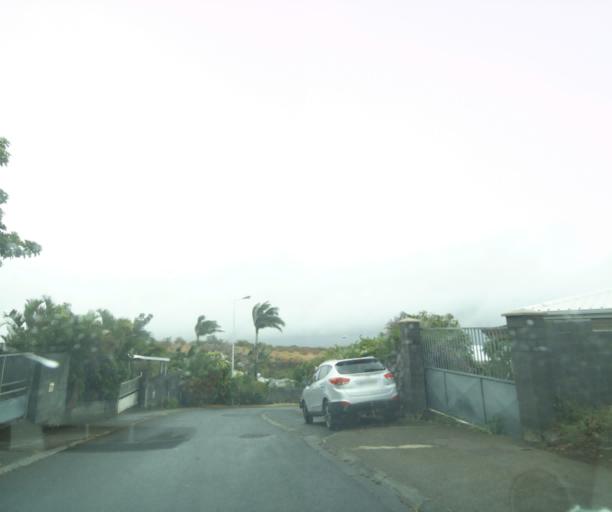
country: RE
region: Reunion
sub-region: Reunion
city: Saint-Paul
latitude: -21.0449
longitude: 55.2539
